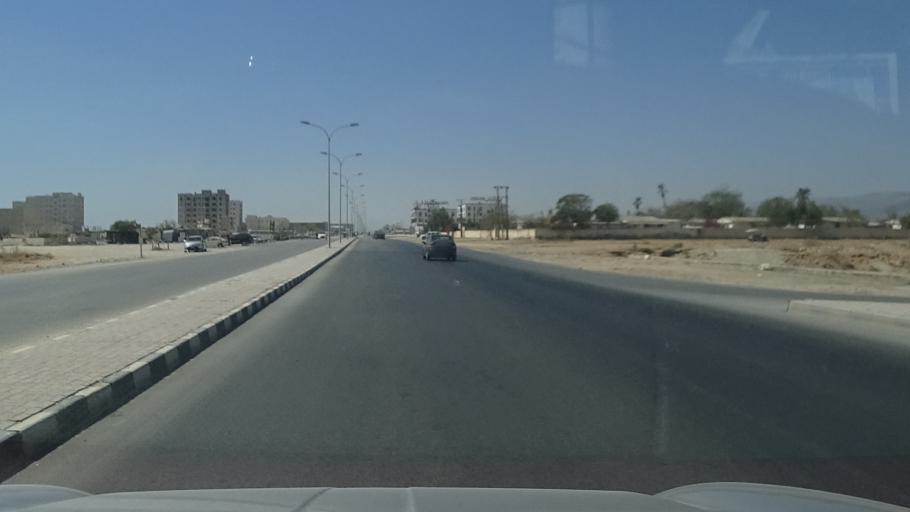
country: OM
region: Zufar
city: Salalah
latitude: 17.0325
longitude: 54.0573
